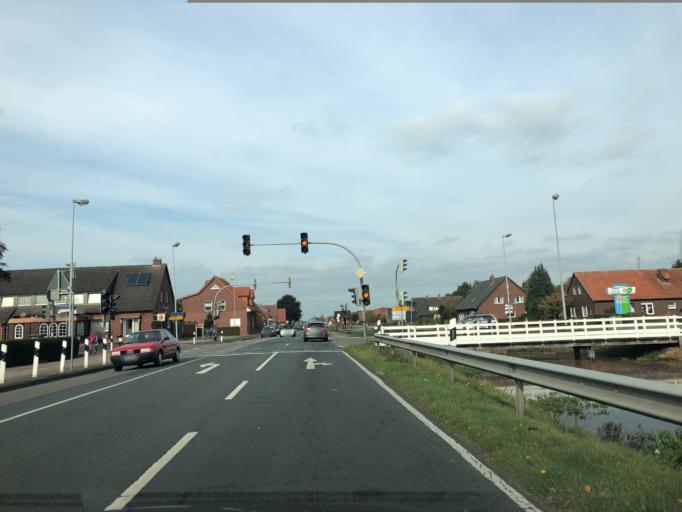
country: DE
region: Lower Saxony
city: Papenburg
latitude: 53.0425
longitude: 7.4657
